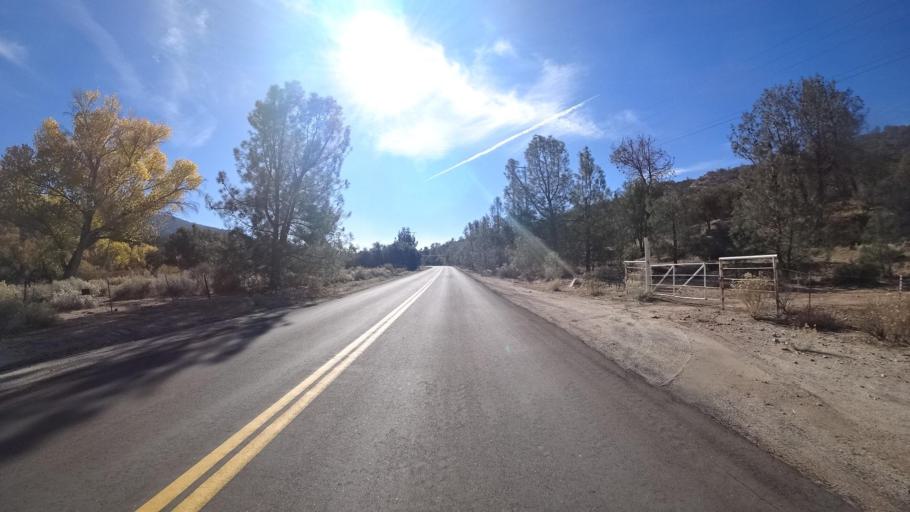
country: US
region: California
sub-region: Kern County
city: Bodfish
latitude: 35.5227
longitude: -118.5111
